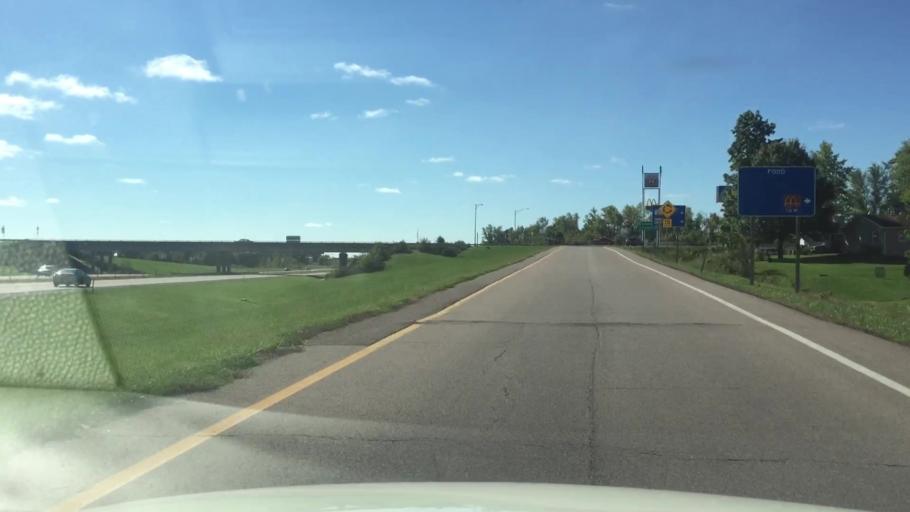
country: US
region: Missouri
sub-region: Boone County
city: Ashland
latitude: 38.7757
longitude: -92.2514
